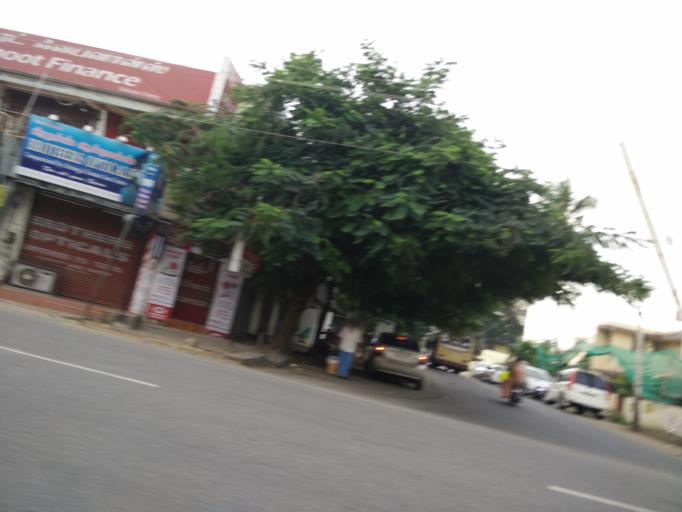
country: IN
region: Tamil Nadu
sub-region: Coimbatore
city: Coimbatore
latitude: 11.0259
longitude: 76.9417
